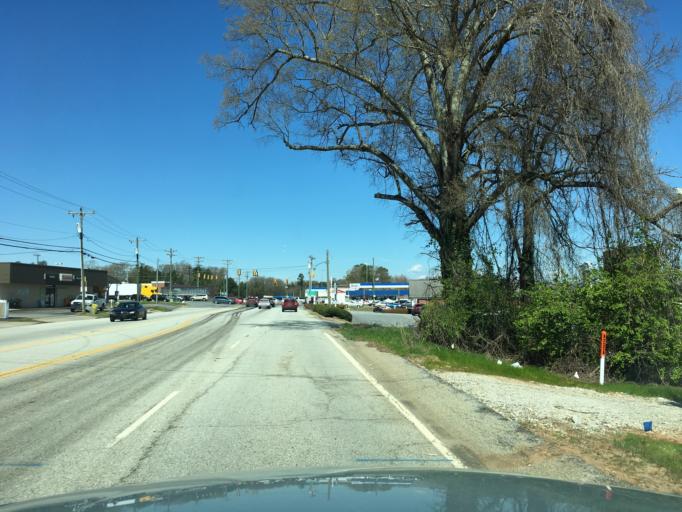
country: US
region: South Carolina
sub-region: Spartanburg County
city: Fairforest
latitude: 34.9343
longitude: -82.0027
